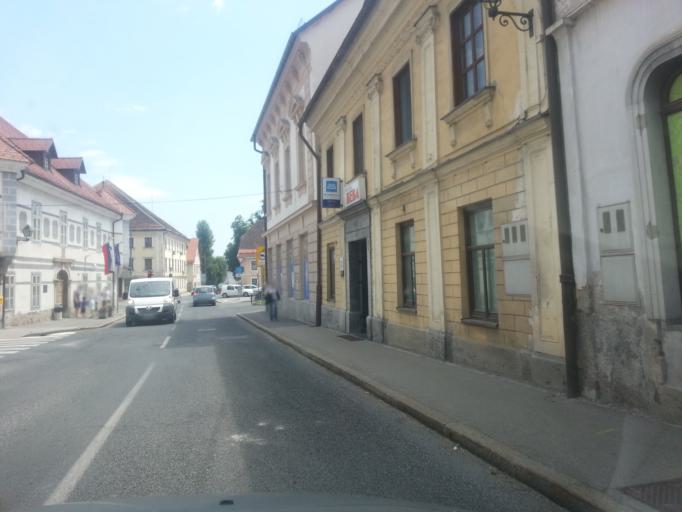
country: SI
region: Vrhnika
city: Vrhnika
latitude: 45.9665
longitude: 14.2975
